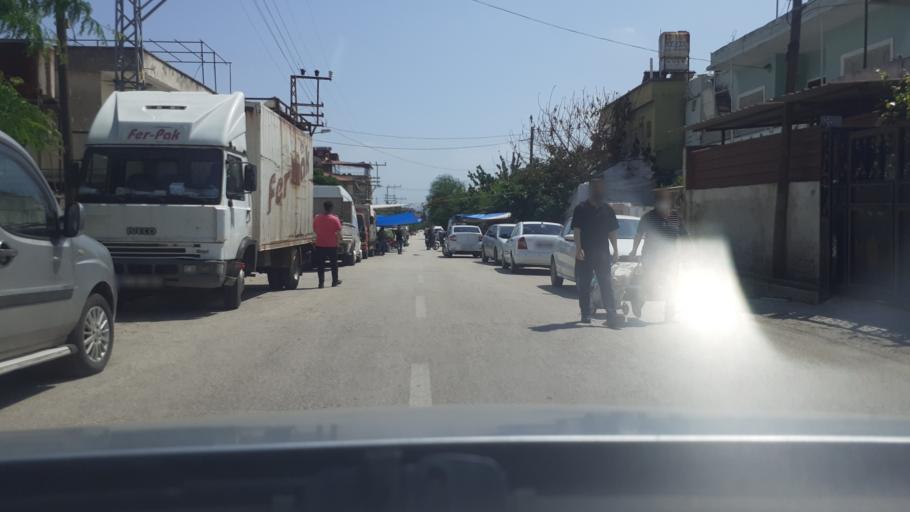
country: TR
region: Hatay
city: Kirikhan
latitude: 36.4928
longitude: 36.3540
